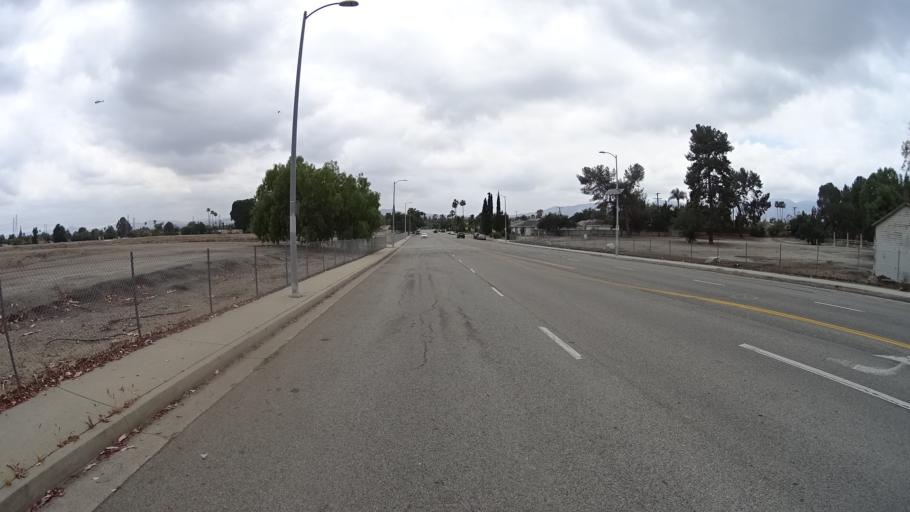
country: US
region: California
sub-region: Los Angeles County
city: San Fernando
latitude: 34.2603
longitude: -118.4455
